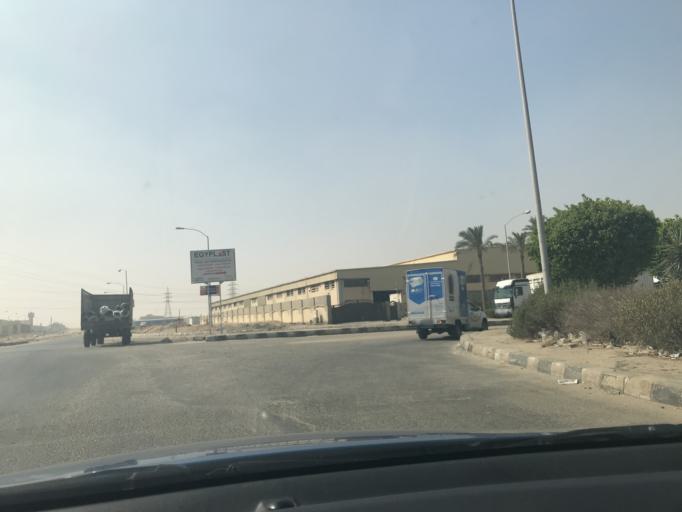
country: EG
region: Eastern Province
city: Bilbays
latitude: 30.2486
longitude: 31.7607
